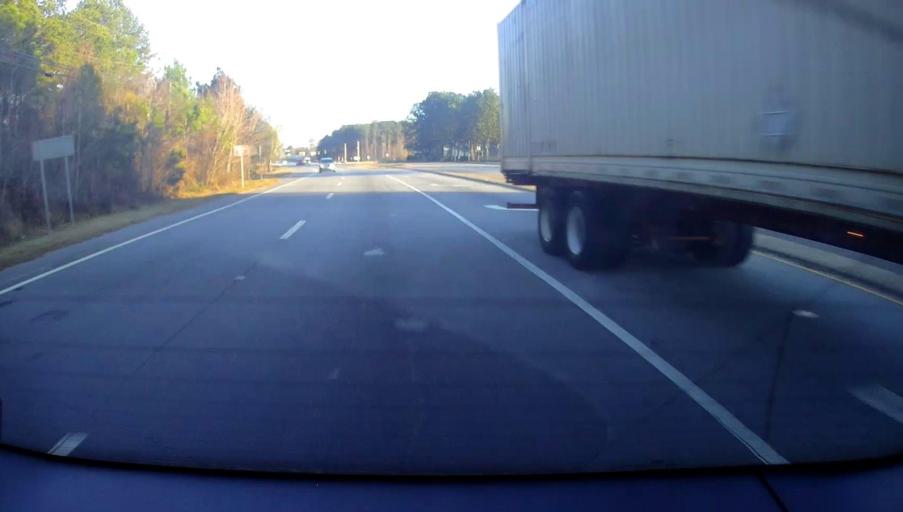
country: US
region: Georgia
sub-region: Fulton County
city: Fairburn
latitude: 33.5564
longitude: -84.5906
